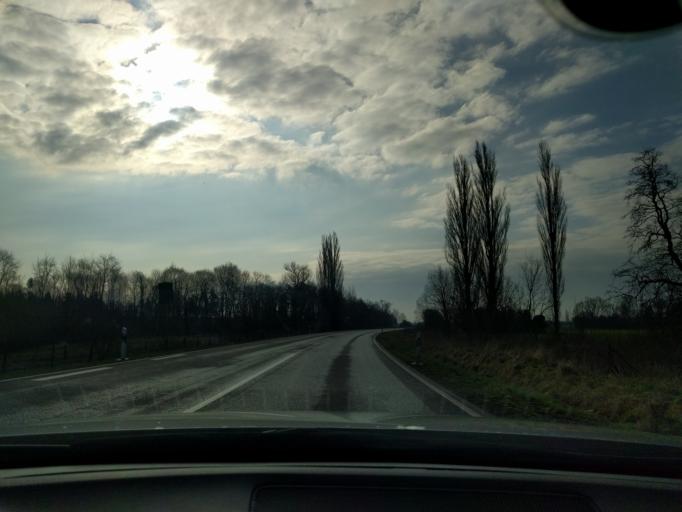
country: DE
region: Saxony-Anhalt
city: Stendal
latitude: 52.6288
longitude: 11.8814
